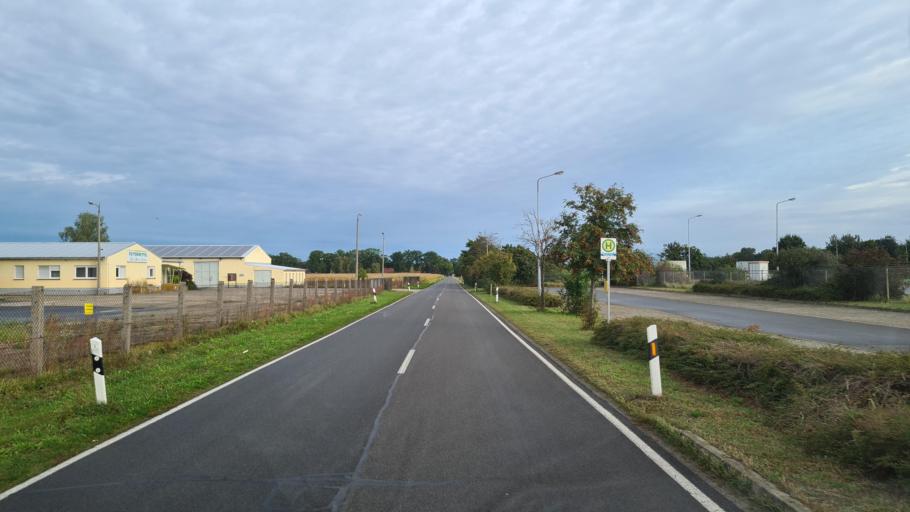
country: DE
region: Brandenburg
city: Kasel-Golzig
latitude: 51.9275
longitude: 13.7079
